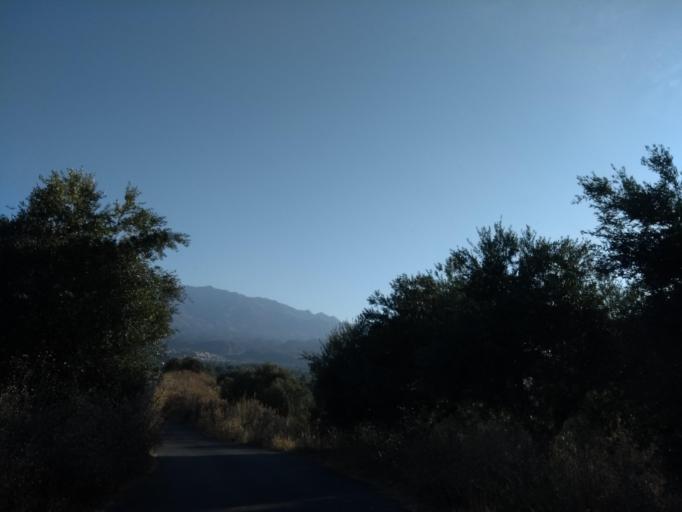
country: GR
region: Crete
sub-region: Nomos Chanias
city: Kalivai
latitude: 35.4460
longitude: 24.1734
